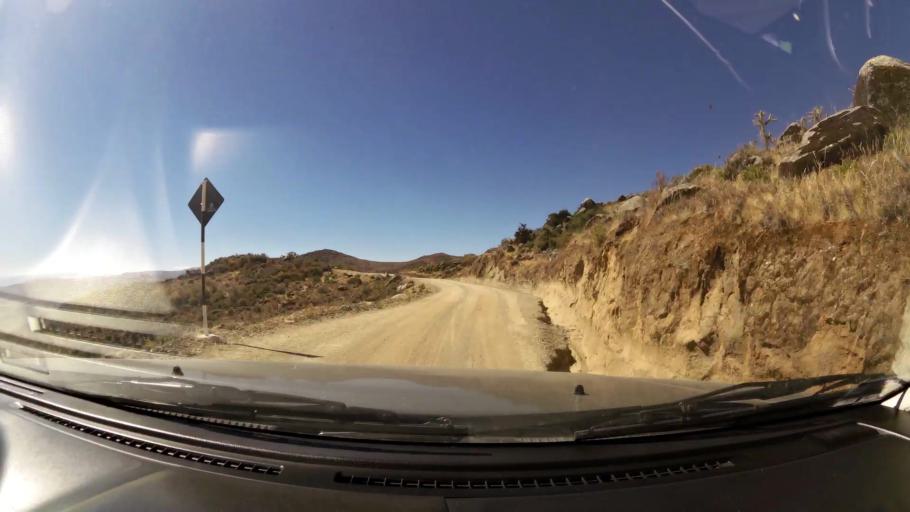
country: PE
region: Huancavelica
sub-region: Huaytara
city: Quito-Arma
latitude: -13.6370
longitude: -75.3675
